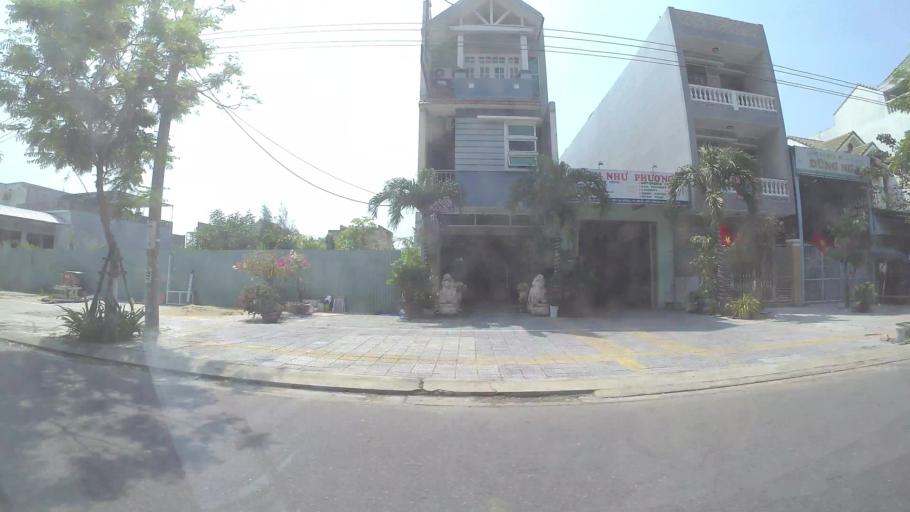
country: VN
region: Da Nang
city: Ngu Hanh Son
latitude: 15.9989
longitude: 108.2674
